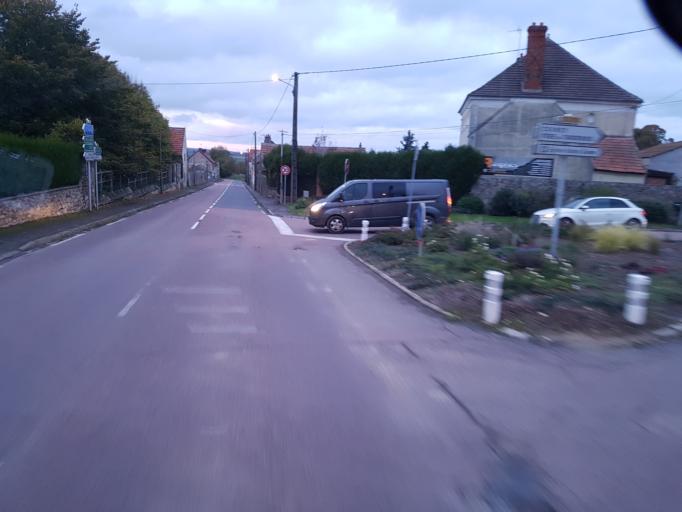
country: FR
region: Picardie
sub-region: Departement de l'Aisne
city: Coincy
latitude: 49.1525
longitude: 3.3873
